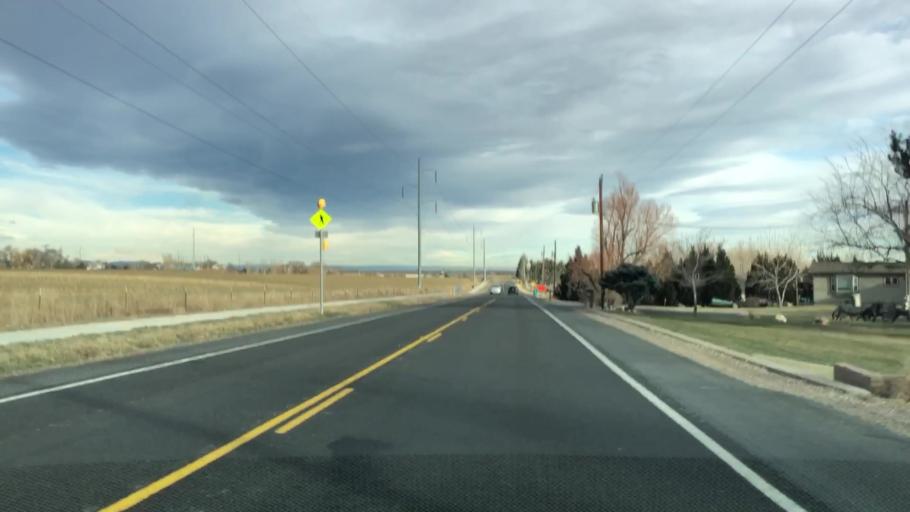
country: US
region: Colorado
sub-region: Larimer County
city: Loveland
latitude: 40.4604
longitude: -105.0441
